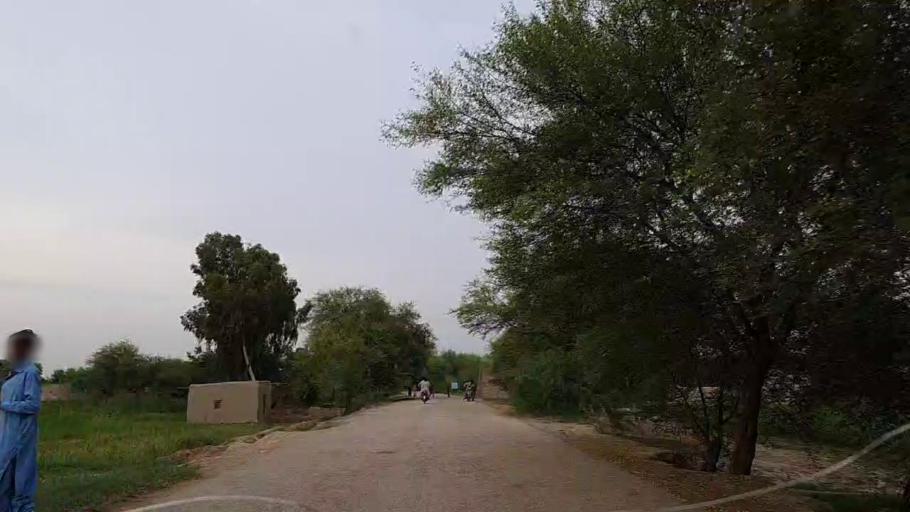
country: PK
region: Sindh
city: Mirpur Mathelo
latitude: 27.8493
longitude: 69.6291
